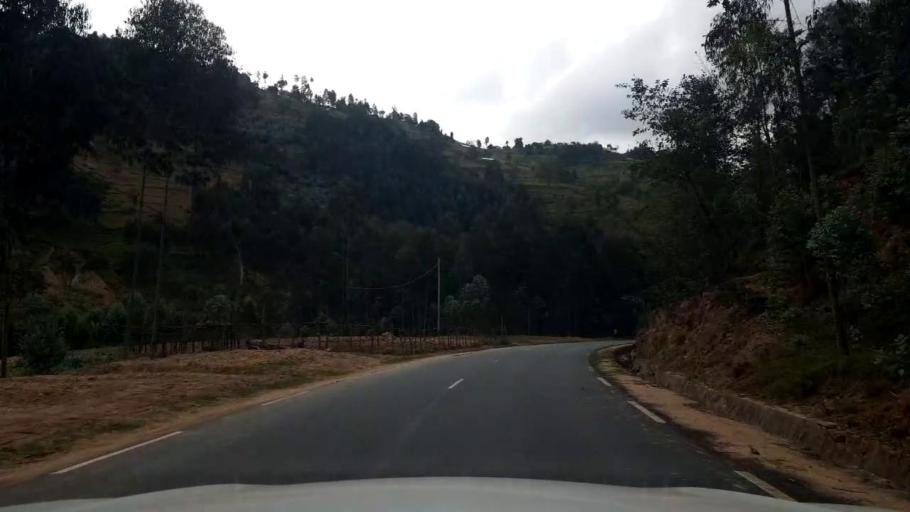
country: RW
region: Northern Province
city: Musanze
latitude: -1.6955
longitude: 29.5569
